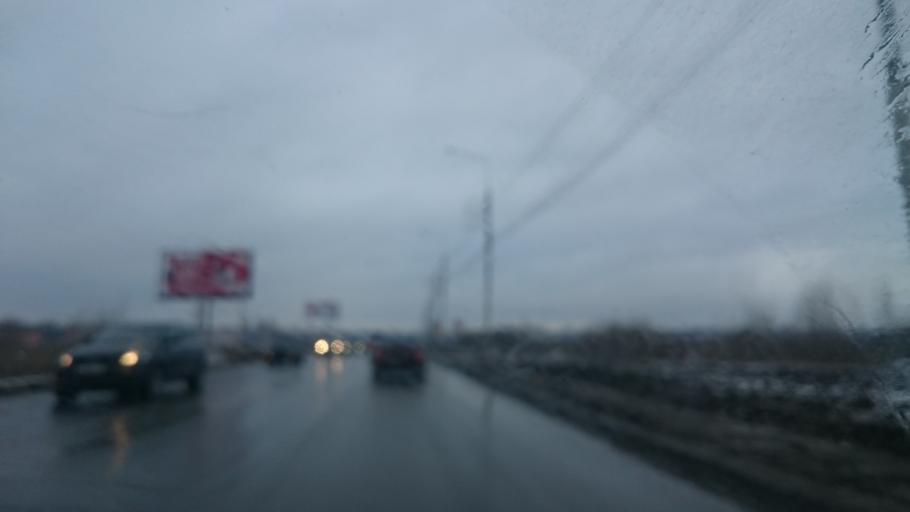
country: RU
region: Tula
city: Tula
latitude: 54.1819
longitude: 37.6492
